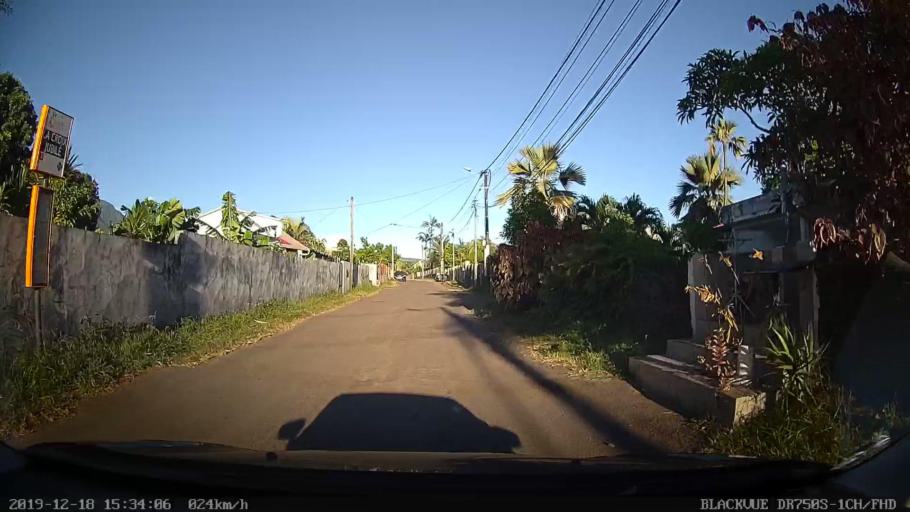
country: RE
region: Reunion
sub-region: Reunion
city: Bras-Panon
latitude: -20.9995
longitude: 55.6660
